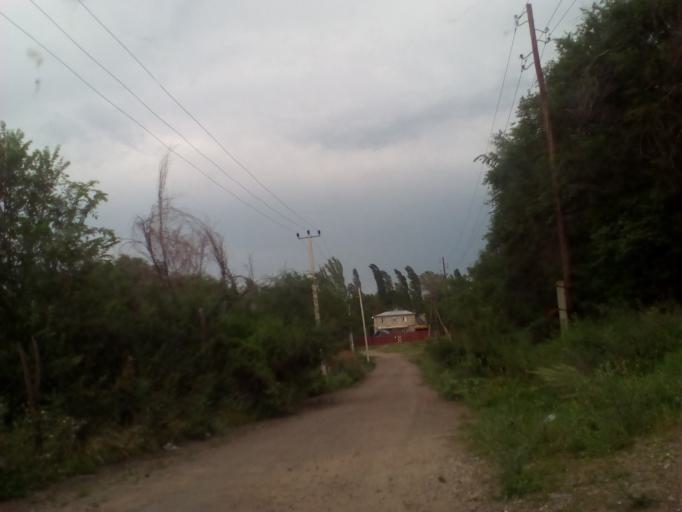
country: KZ
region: Almaty Oblysy
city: Burunday
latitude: 43.1565
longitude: 76.4037
